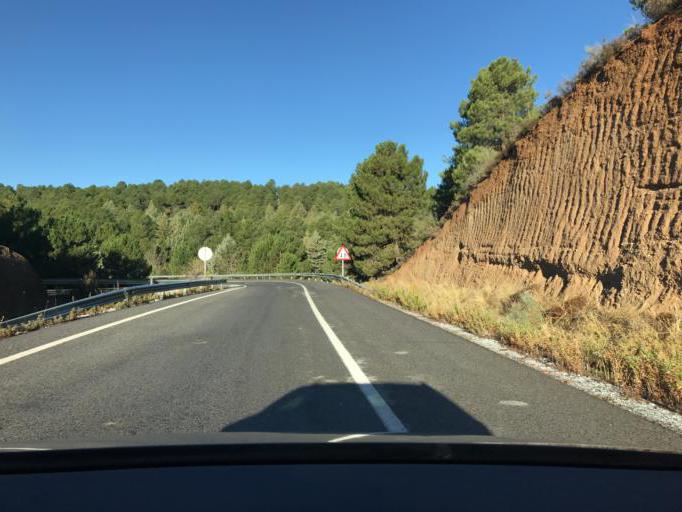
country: ES
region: Andalusia
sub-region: Provincia de Granada
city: Huetor Santillan
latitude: 37.2275
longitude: -3.5312
